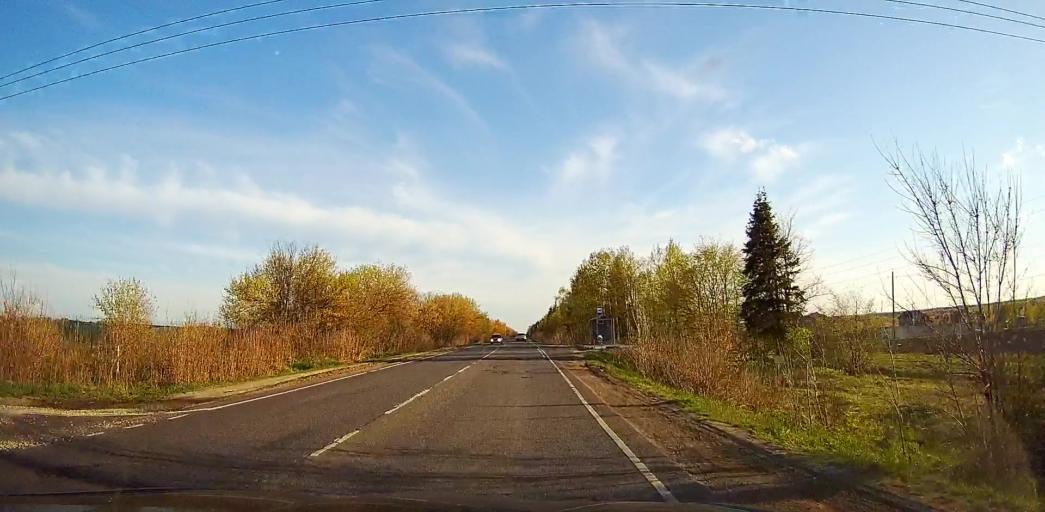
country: RU
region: Moskovskaya
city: Bronnitsy
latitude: 55.3193
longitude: 38.2175
